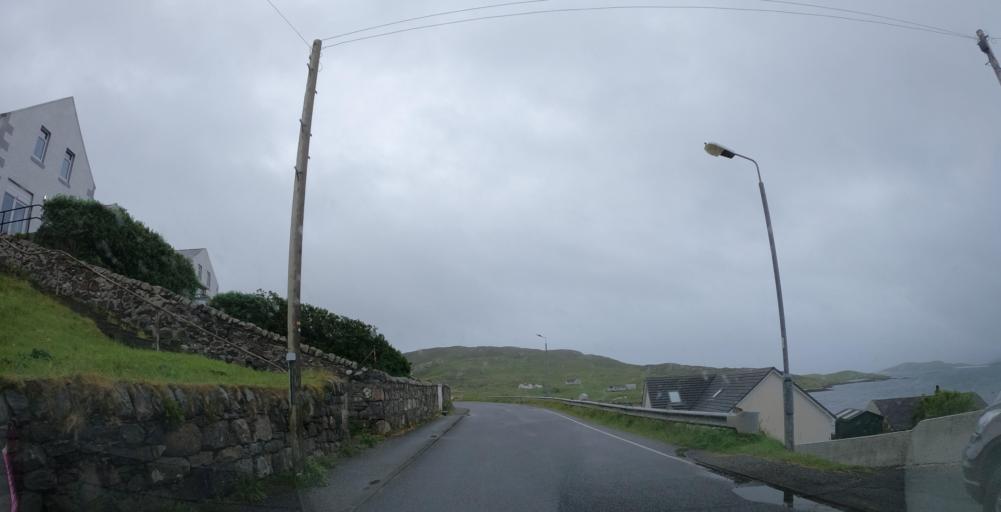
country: GB
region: Scotland
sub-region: Eilean Siar
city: Barra
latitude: 56.9547
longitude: -7.4851
